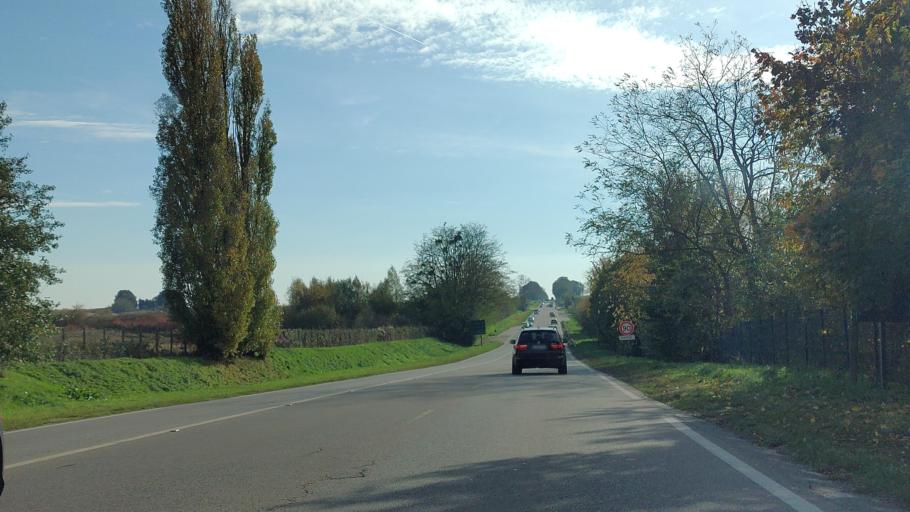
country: FR
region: Ile-de-France
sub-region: Departement du Val-d'Oise
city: Survilliers
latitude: 49.0882
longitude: 2.5302
